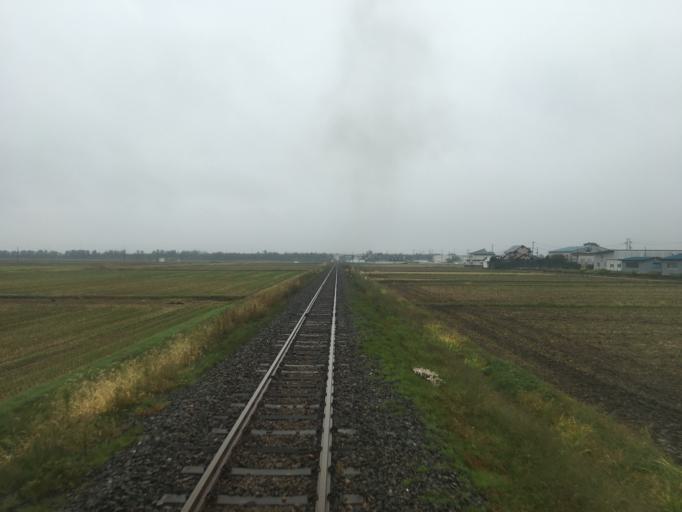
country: JP
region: Miyagi
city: Furukawa
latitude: 38.5737
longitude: 140.9177
